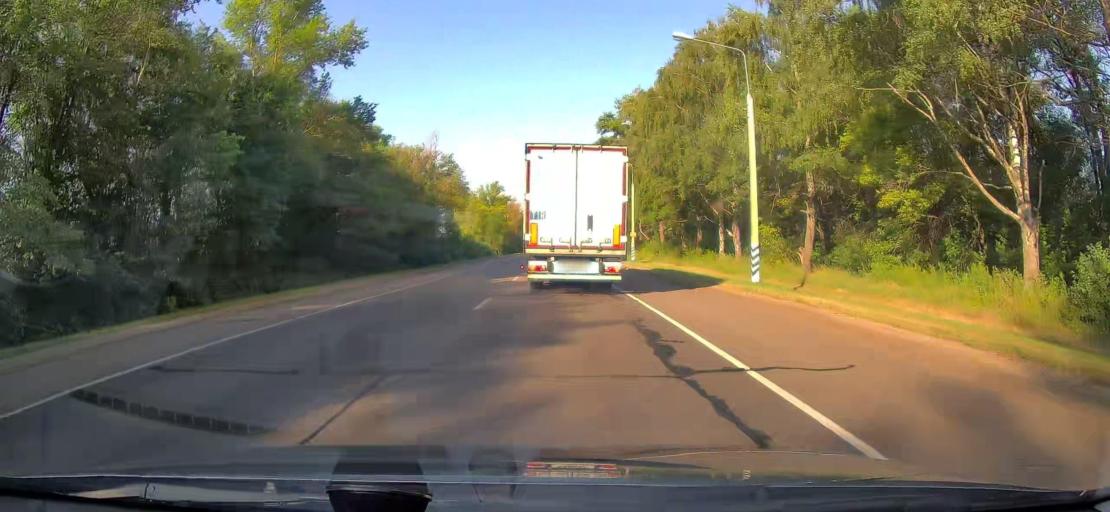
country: RU
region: Tula
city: Chern'
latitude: 53.4581
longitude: 36.9354
